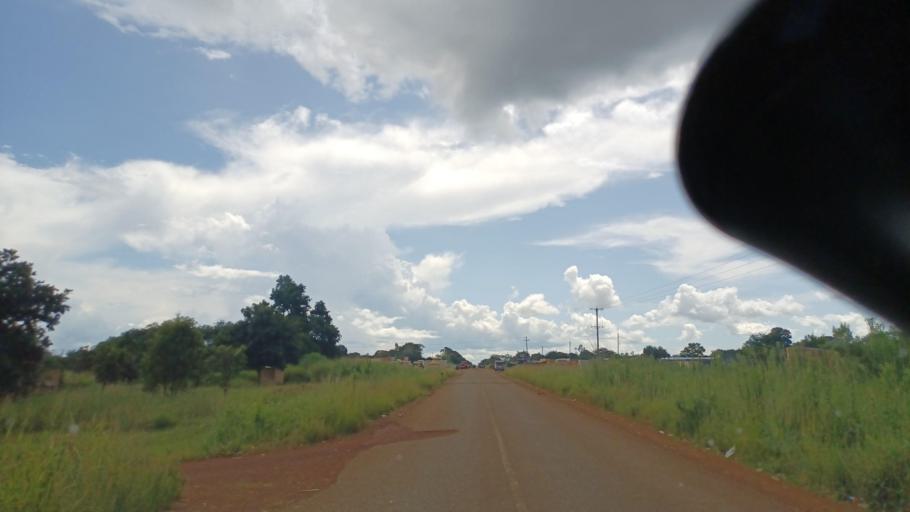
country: ZM
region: North-Western
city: Kasempa
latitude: -13.1038
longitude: 25.8728
